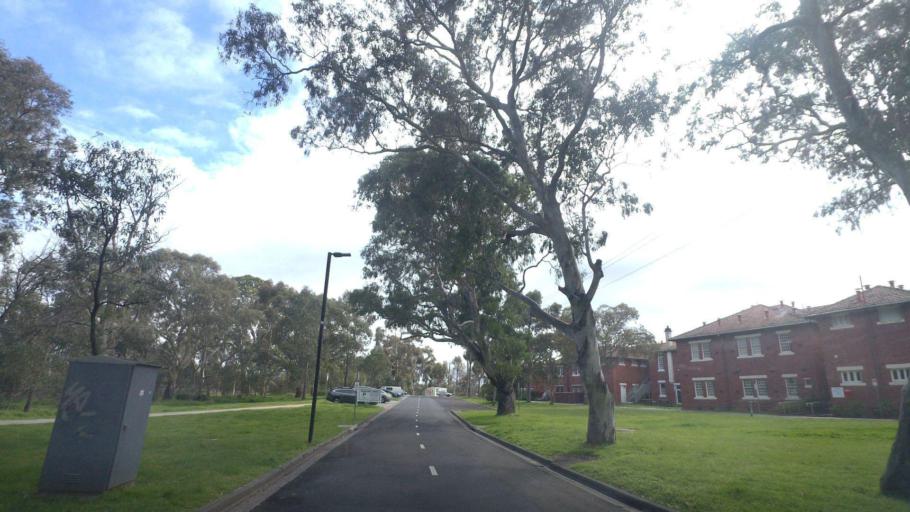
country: AU
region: Victoria
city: Macleod
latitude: -37.7217
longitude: 145.0571
